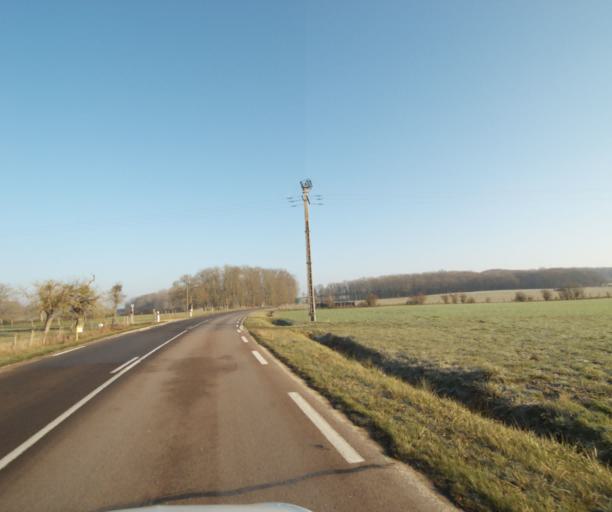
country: FR
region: Champagne-Ardenne
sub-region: Departement de la Haute-Marne
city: Montier-en-Der
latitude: 48.4476
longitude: 4.7361
